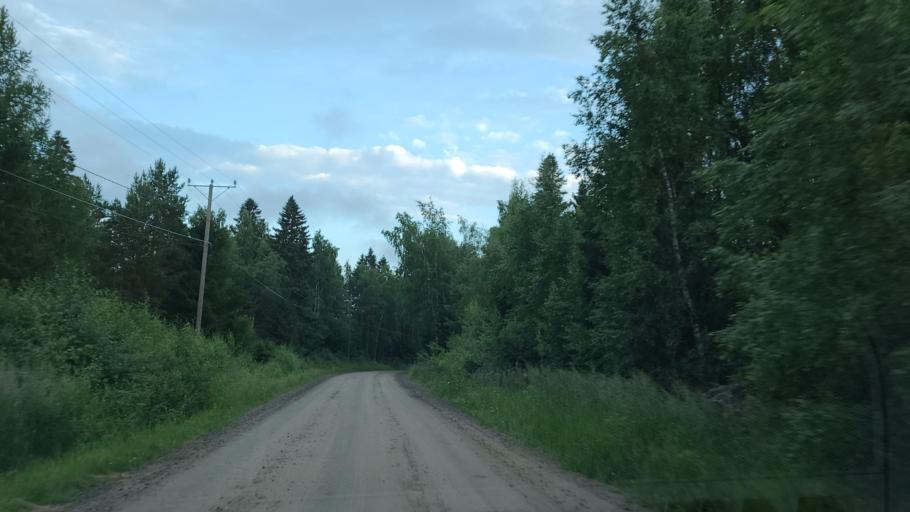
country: FI
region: Ostrobothnia
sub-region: Vaasa
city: Replot
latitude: 63.3098
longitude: 21.1579
